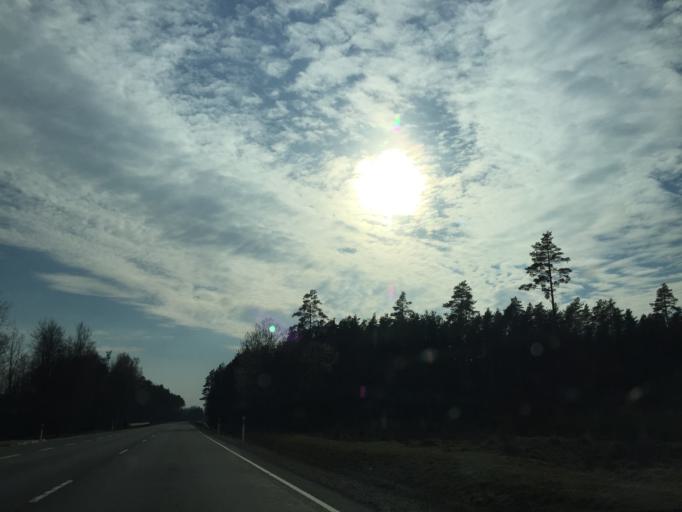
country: EE
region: Jogevamaa
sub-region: Mustvee linn
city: Mustvee
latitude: 58.9591
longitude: 27.0835
